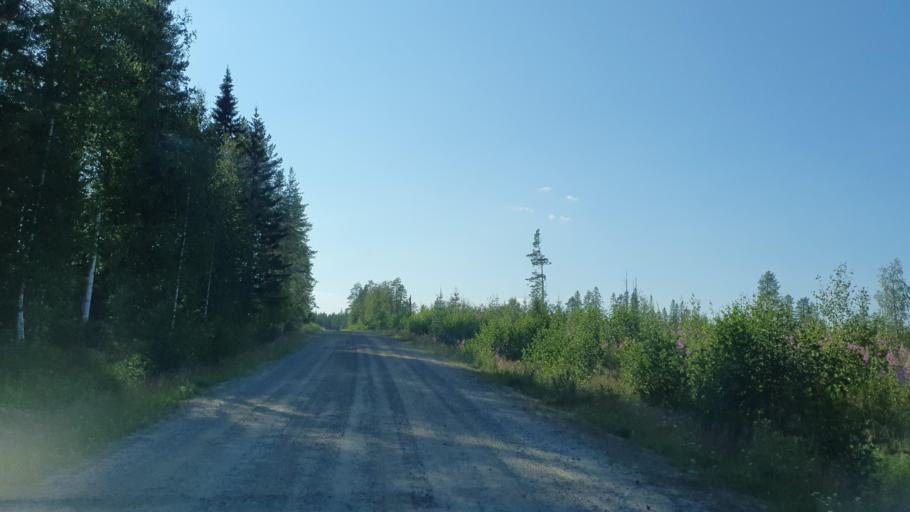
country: FI
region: Kainuu
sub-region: Kehys-Kainuu
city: Kuhmo
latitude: 64.0315
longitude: 29.6897
